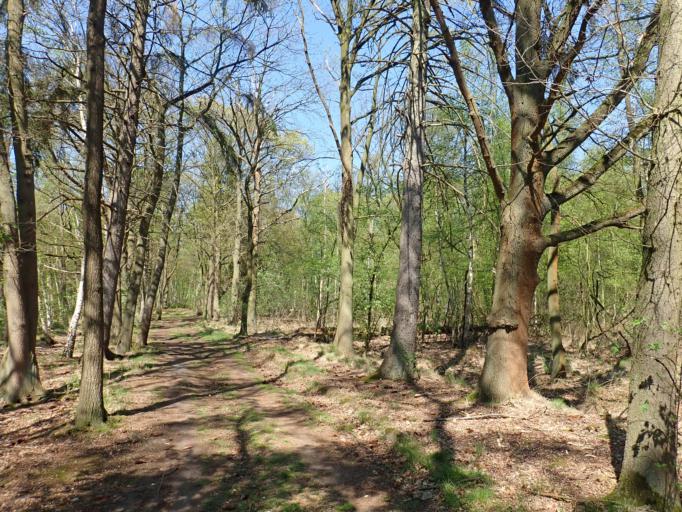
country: BE
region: Flanders
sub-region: Provincie Antwerpen
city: Brasschaat
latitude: 51.3328
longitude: 4.5167
